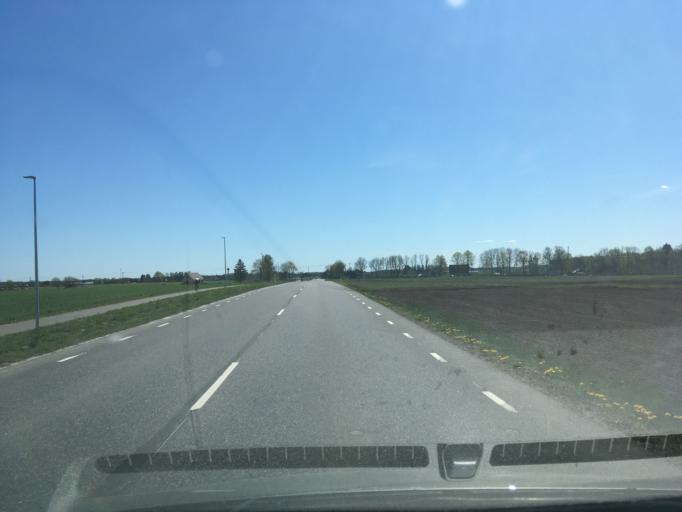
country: EE
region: Harju
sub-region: Maardu linn
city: Maardu
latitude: 59.4426
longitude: 25.0705
